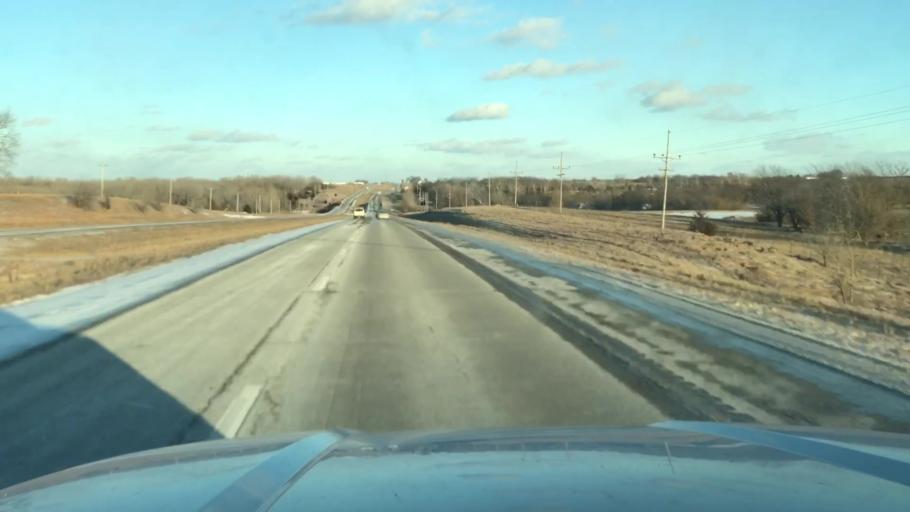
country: US
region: Missouri
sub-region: Clinton County
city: Cameron
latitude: 39.7546
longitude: -94.3257
